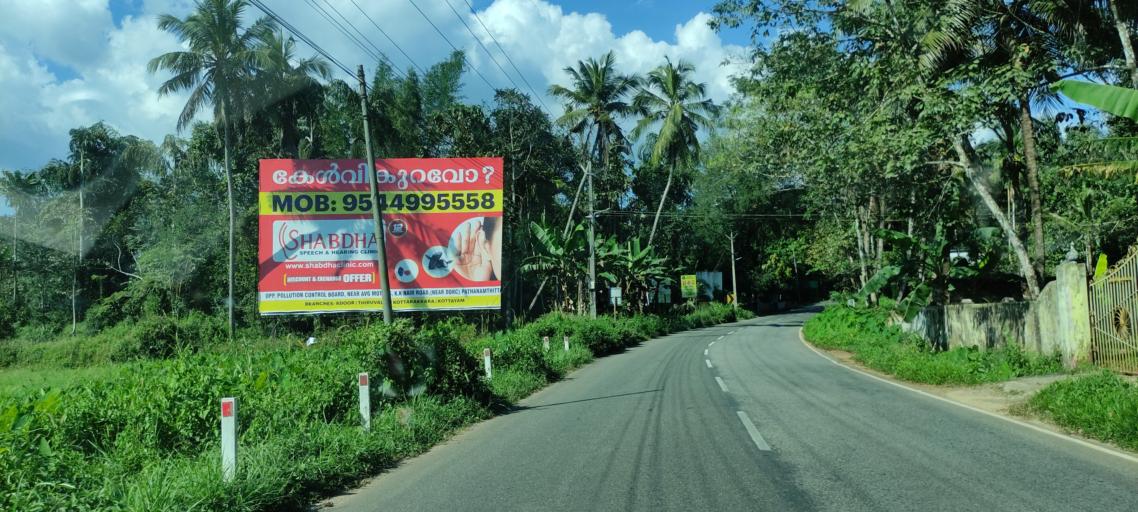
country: IN
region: Kerala
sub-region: Pattanamtitta
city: Adur
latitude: 9.2183
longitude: 76.7489
